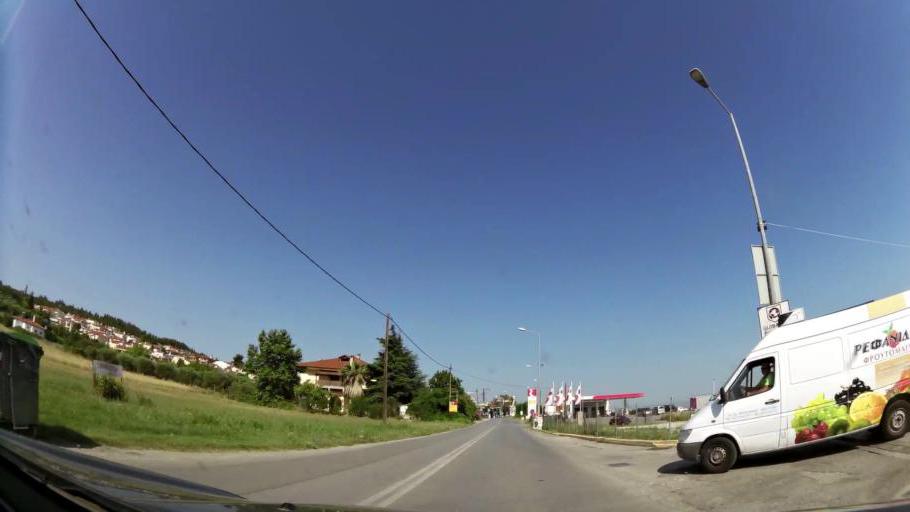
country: GR
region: Central Macedonia
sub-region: Nomos Thessalonikis
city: Neo Rysi
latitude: 40.4968
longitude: 22.9934
